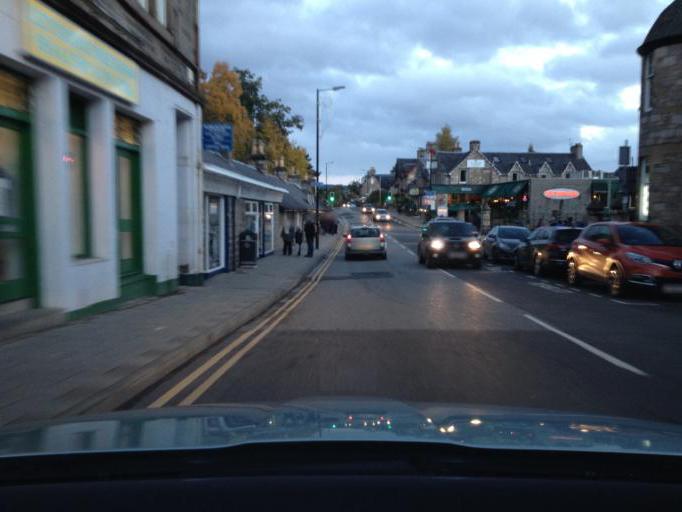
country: GB
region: Scotland
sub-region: Perth and Kinross
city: Pitlochry
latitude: 56.7026
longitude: -3.7328
